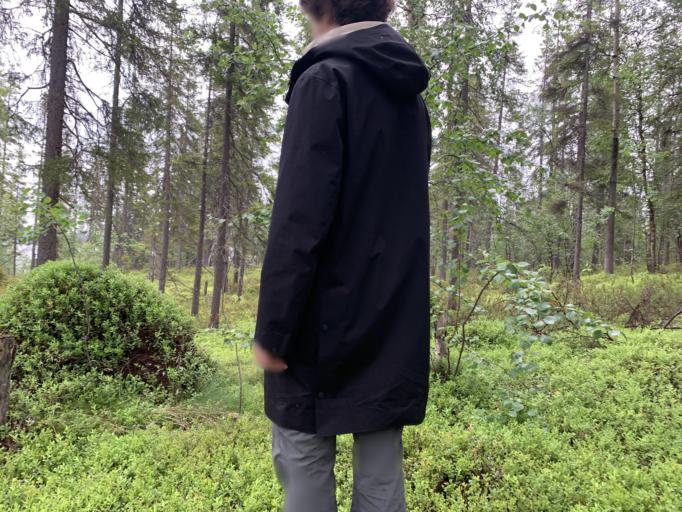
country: RU
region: Murmansk
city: Afrikanda
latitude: 67.6601
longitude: 32.9133
